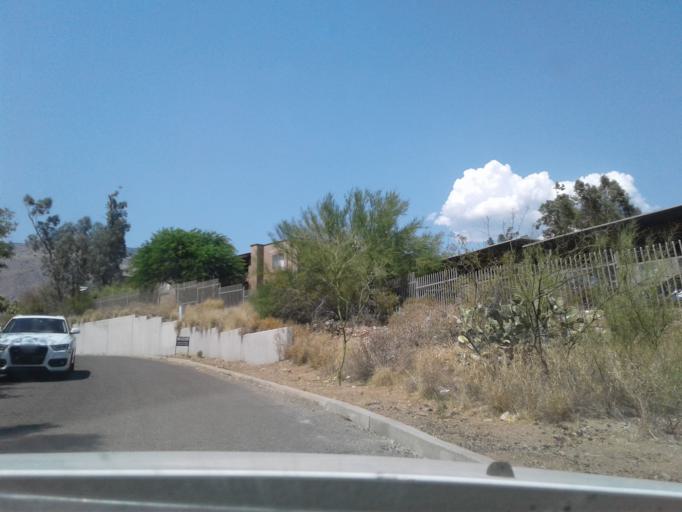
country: US
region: Arizona
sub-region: Pima County
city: Catalina Foothills
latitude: 32.3094
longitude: -110.8896
